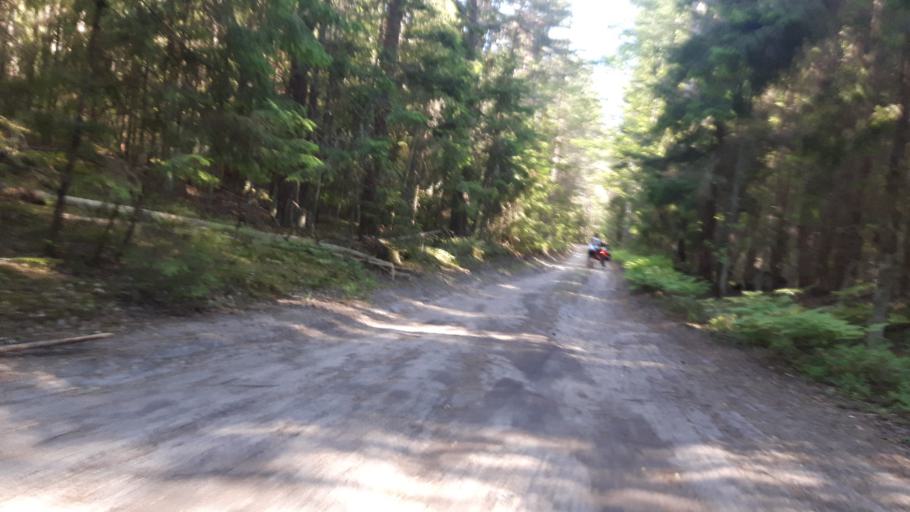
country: LV
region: Salacgrivas
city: Salacgriva
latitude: 57.7239
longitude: 24.3486
